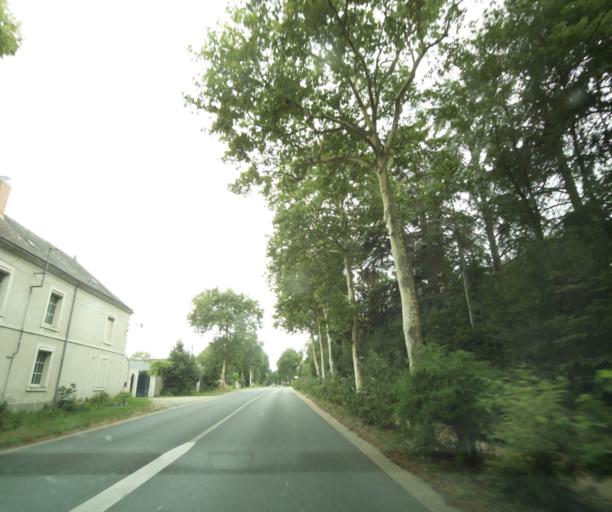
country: FR
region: Pays de la Loire
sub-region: Departement de Maine-et-Loire
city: Pellouailles-les-Vignes
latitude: 47.5214
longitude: -0.4445
